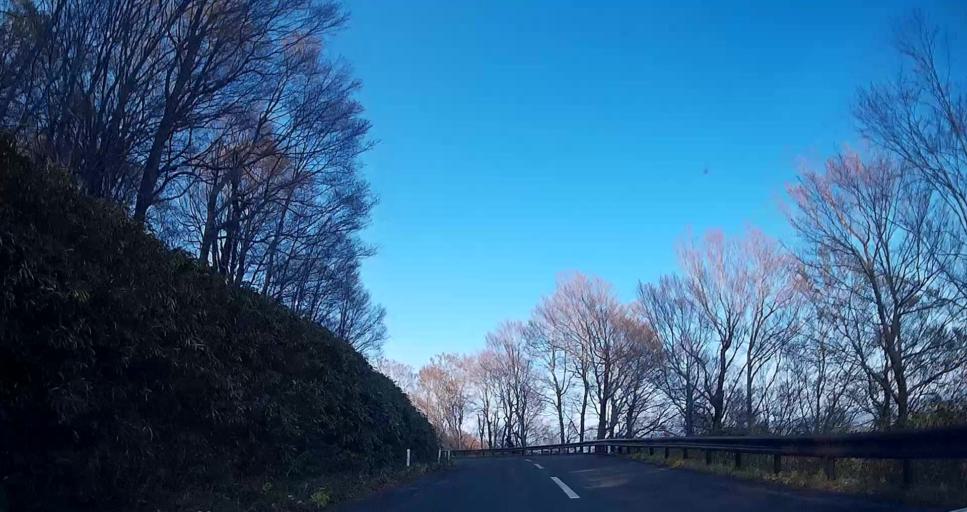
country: JP
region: Aomori
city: Mutsu
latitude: 41.3052
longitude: 141.1156
